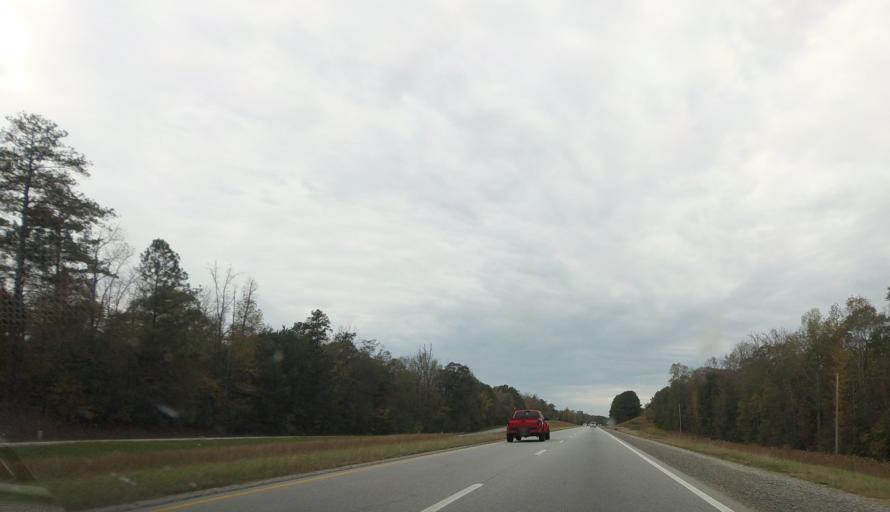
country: US
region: Alabama
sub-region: Lee County
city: Opelika
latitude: 32.6358
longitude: -85.2966
